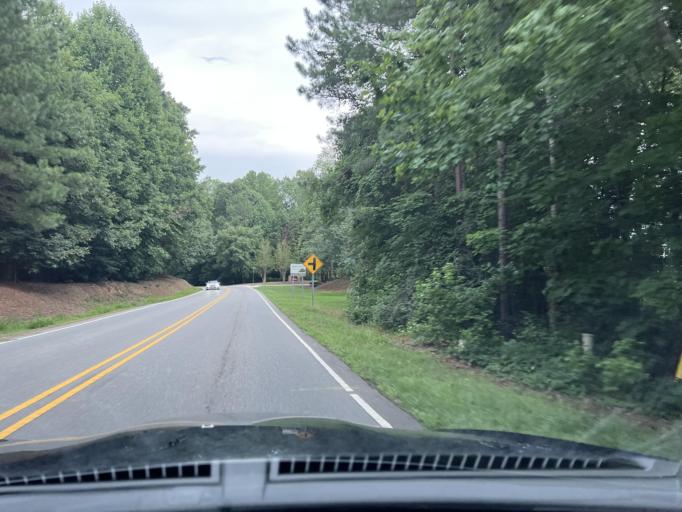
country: US
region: North Carolina
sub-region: Wake County
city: Wake Forest
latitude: 36.0118
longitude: -78.5460
